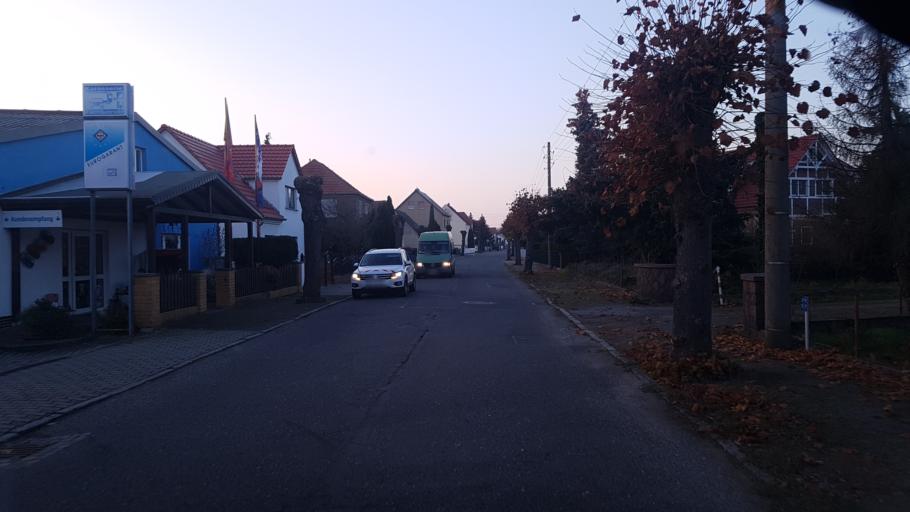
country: DE
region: Brandenburg
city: Lauchhammer
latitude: 51.4722
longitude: 13.7341
